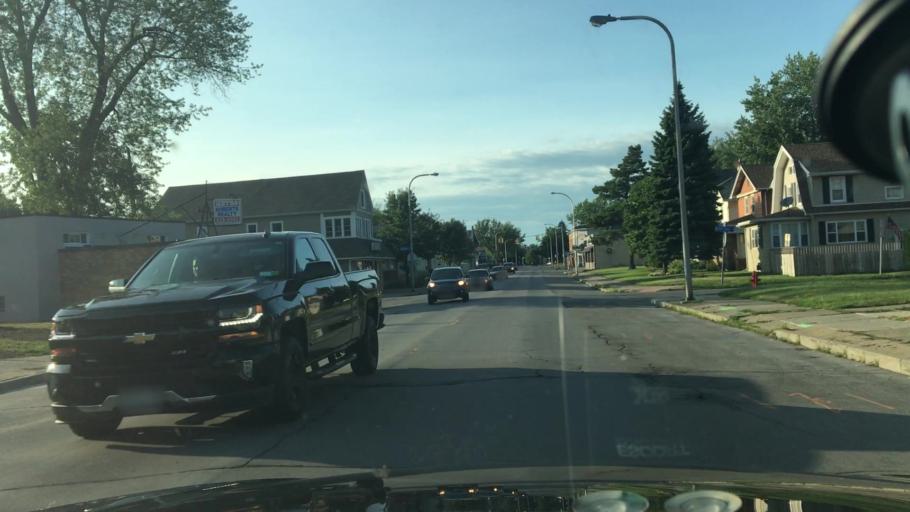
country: US
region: New York
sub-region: Erie County
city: West Seneca
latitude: 42.8406
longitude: -78.8083
